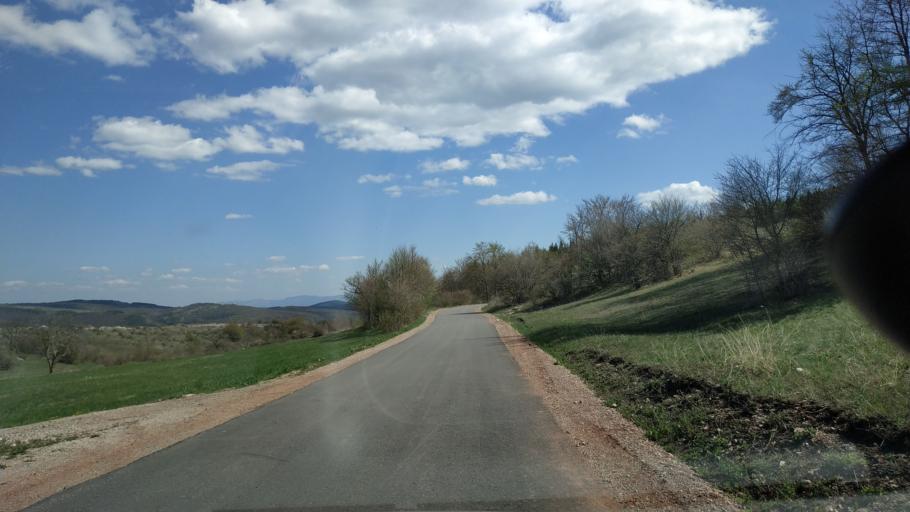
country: RS
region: Central Serbia
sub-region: Zajecarski Okrug
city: Soko Banja
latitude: 43.5828
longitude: 21.8924
